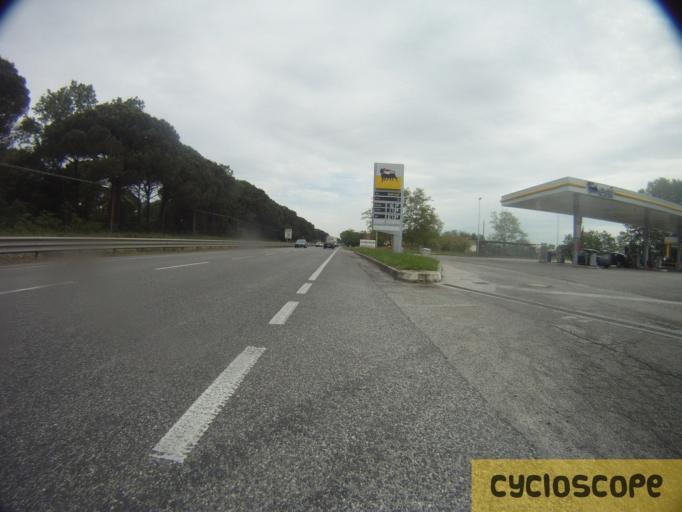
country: IT
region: Emilia-Romagna
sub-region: Provincia di Ferrara
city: Mesola
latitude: 44.9064
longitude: 12.2300
